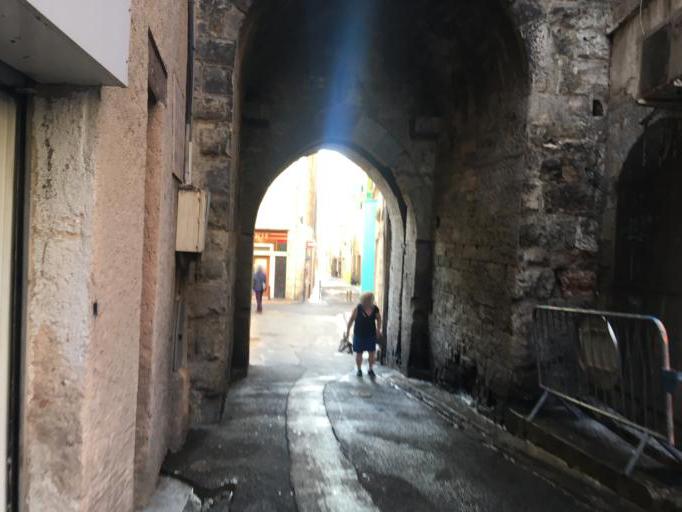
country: FR
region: Provence-Alpes-Cote d'Azur
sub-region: Departement du Var
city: Draguignan
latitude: 43.5388
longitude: 6.4662
